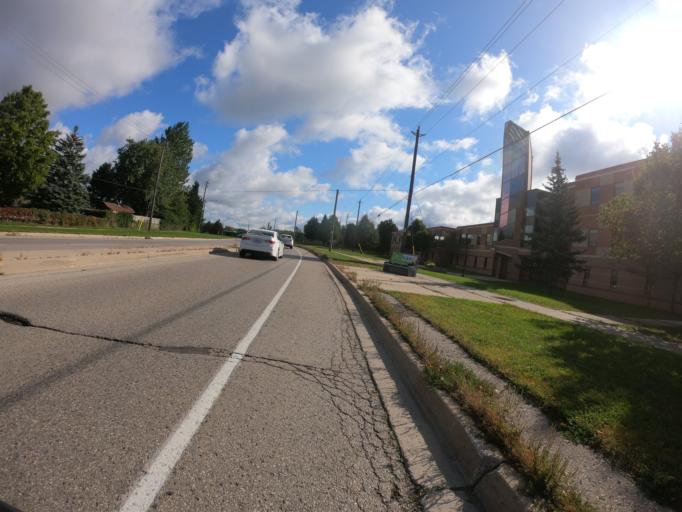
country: CA
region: Ontario
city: Kitchener
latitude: 43.4409
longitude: -80.5477
